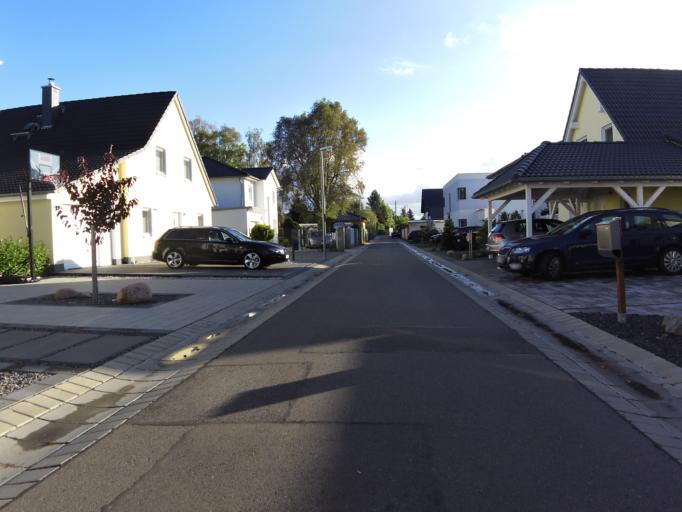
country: DE
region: Saxony
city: Taucha
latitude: 51.3250
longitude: 12.4741
